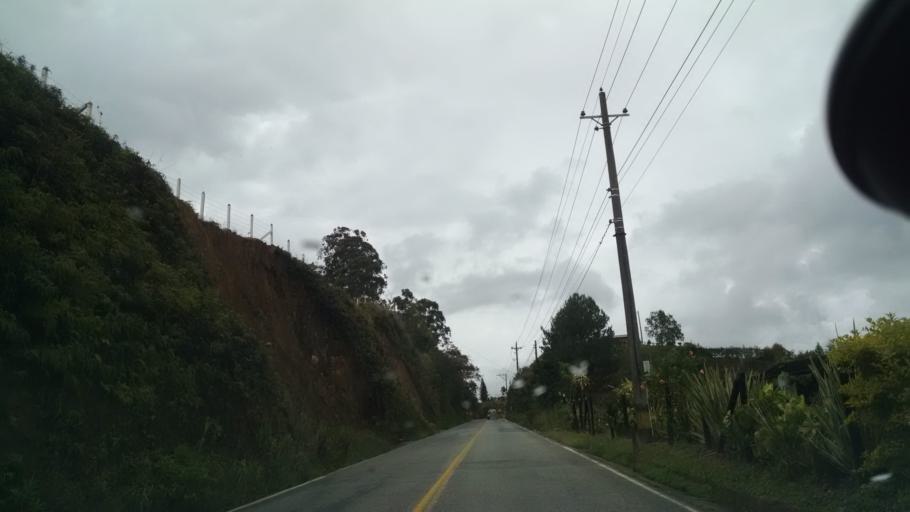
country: CO
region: Antioquia
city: Guatape
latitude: 6.2031
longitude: -75.2089
